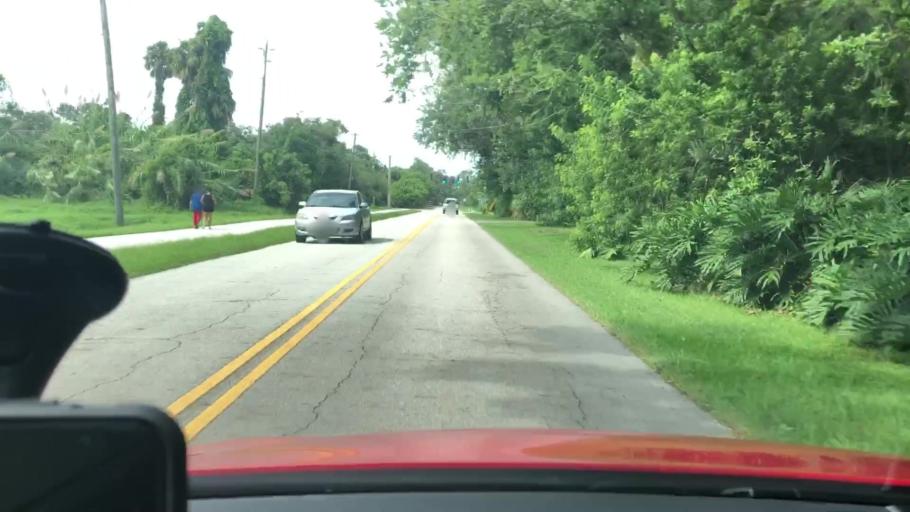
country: US
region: Florida
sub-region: Volusia County
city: South Daytona
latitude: 29.1880
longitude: -81.0090
